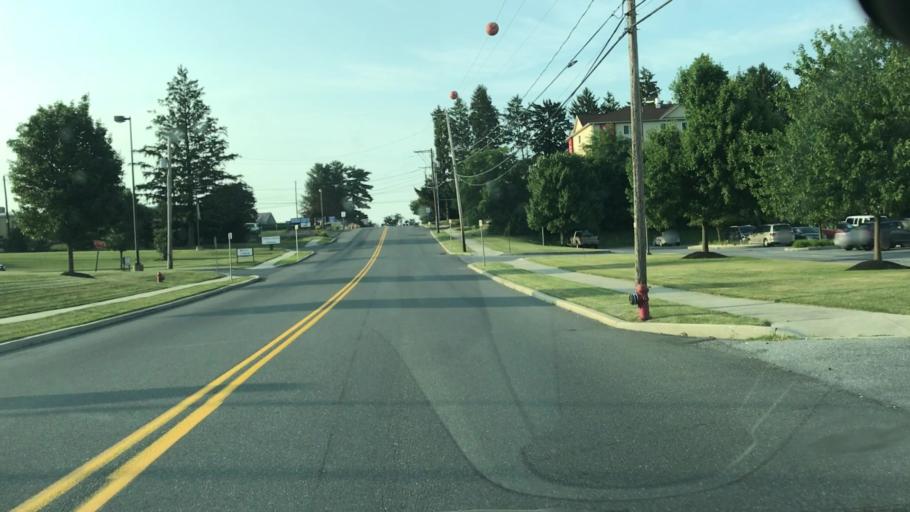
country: US
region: Pennsylvania
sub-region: Dauphin County
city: Progress
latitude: 40.2773
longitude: -76.8219
